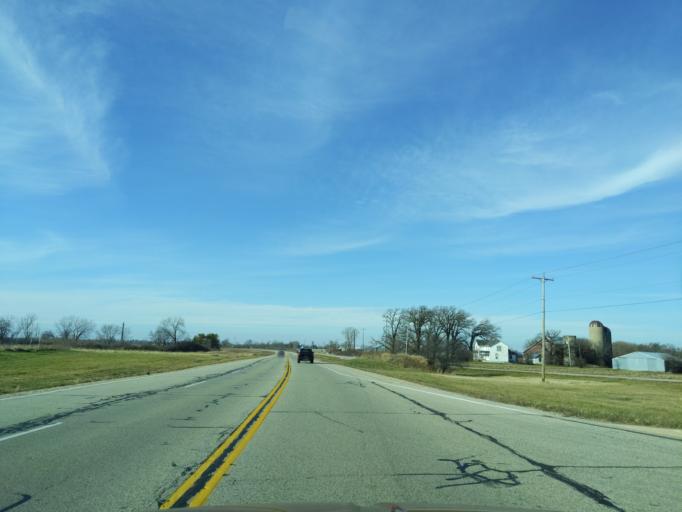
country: US
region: Wisconsin
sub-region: Walworth County
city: Whitewater
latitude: 42.8154
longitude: -88.6900
